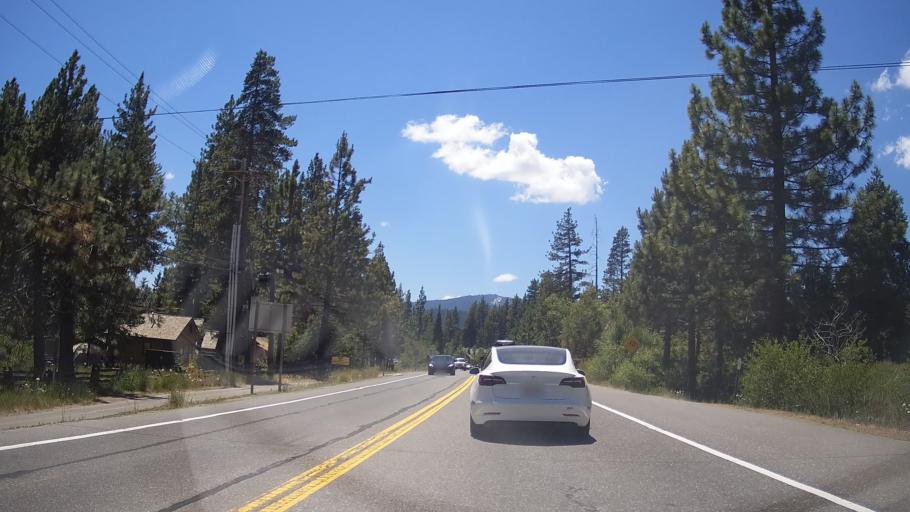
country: US
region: California
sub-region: Placer County
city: Sunnyside-Tahoe City
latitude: 39.1761
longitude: -120.1353
